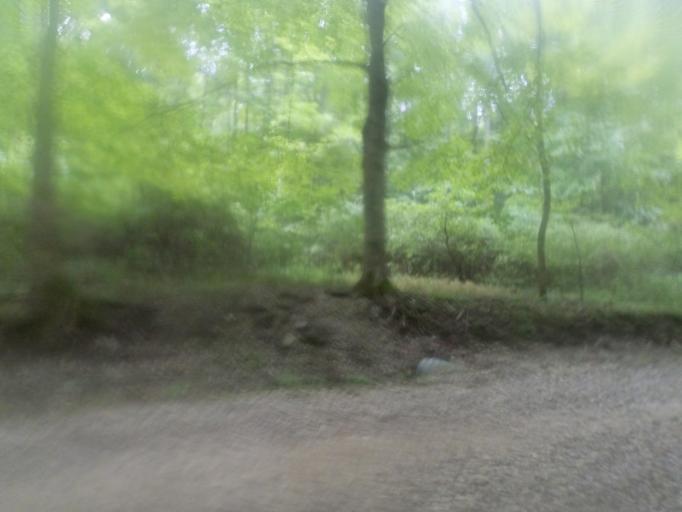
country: US
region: West Virginia
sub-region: Cabell County
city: Huntington
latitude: 38.3792
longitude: -82.4132
